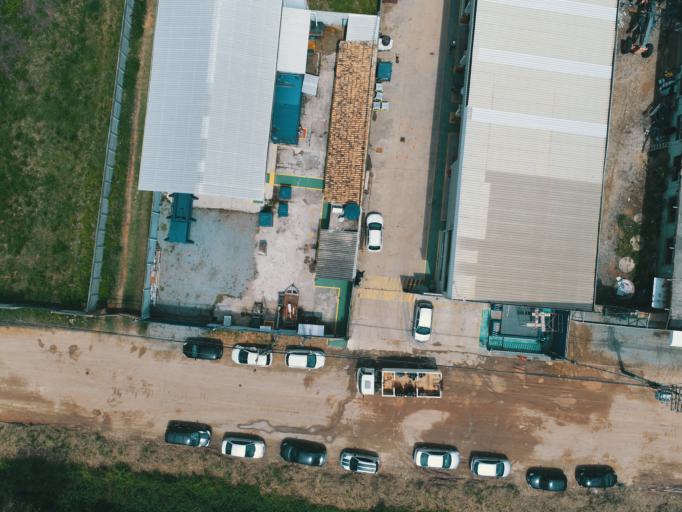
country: BR
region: Rio de Janeiro
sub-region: Macae
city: Macae
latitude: -22.4384
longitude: -41.8701
